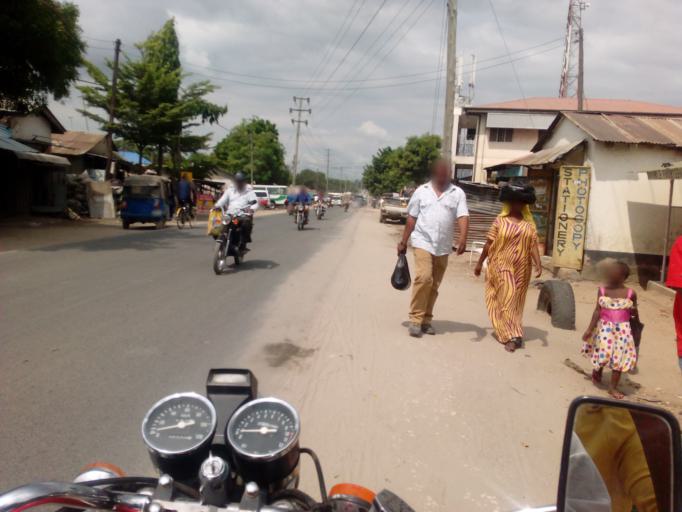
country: TZ
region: Dar es Salaam
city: Dar es Salaam
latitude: -6.8561
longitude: 39.2546
